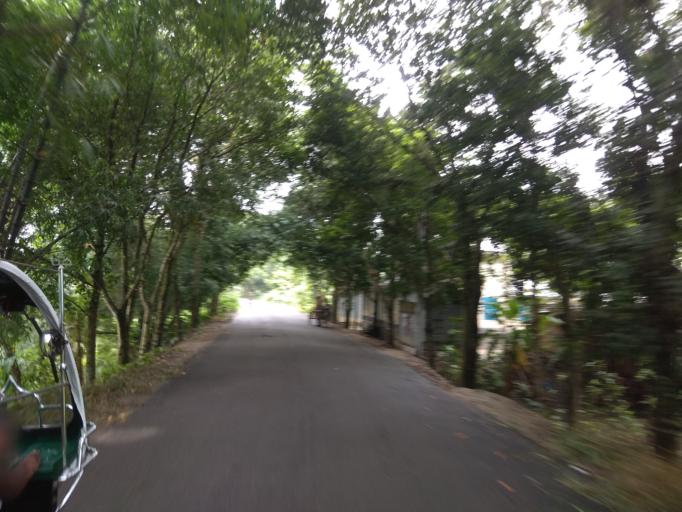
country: BD
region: Dhaka
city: Dohar
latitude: 23.4443
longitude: 90.0638
